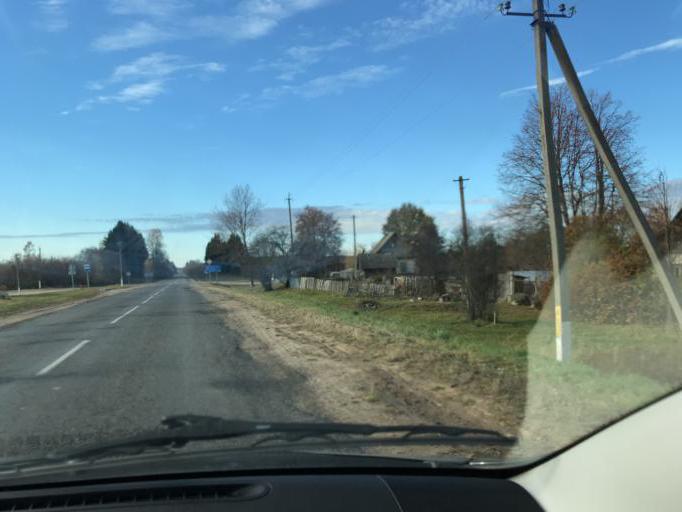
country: BY
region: Vitebsk
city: Haradok
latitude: 55.3725
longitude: 29.6277
